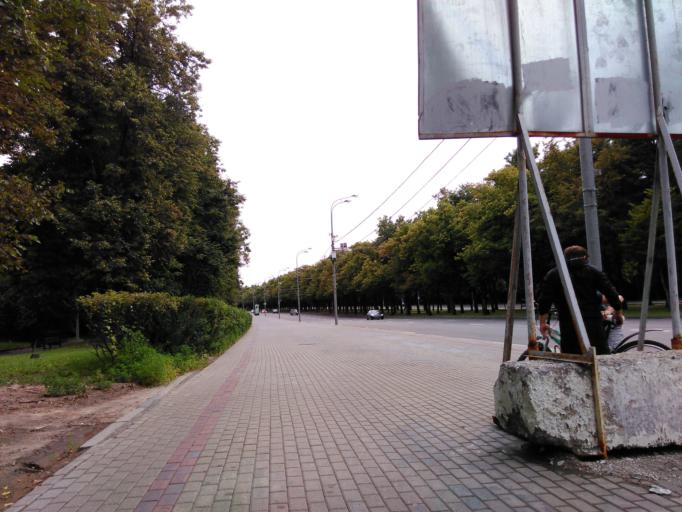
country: RU
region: Moscow
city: Vorob'yovo
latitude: 55.7137
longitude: 37.5373
